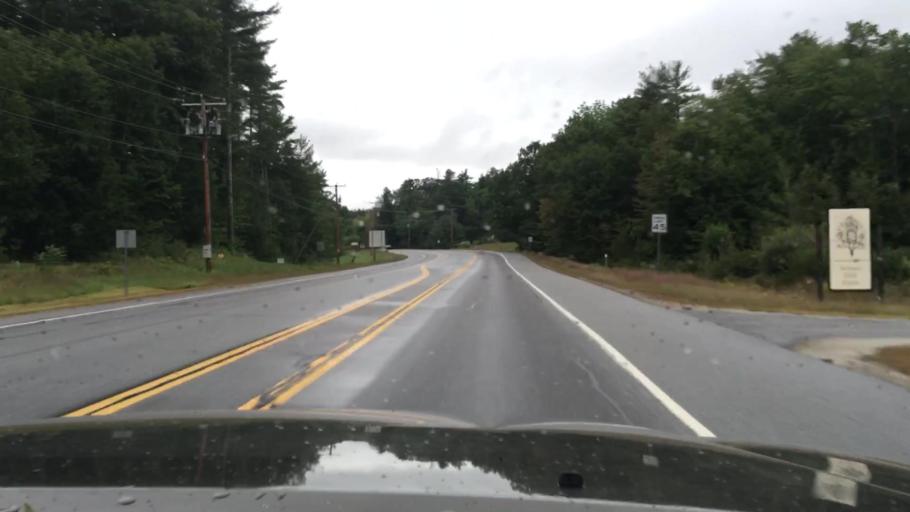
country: US
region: New Hampshire
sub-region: Hillsborough County
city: Hillsborough
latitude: 43.1149
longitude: -71.9498
